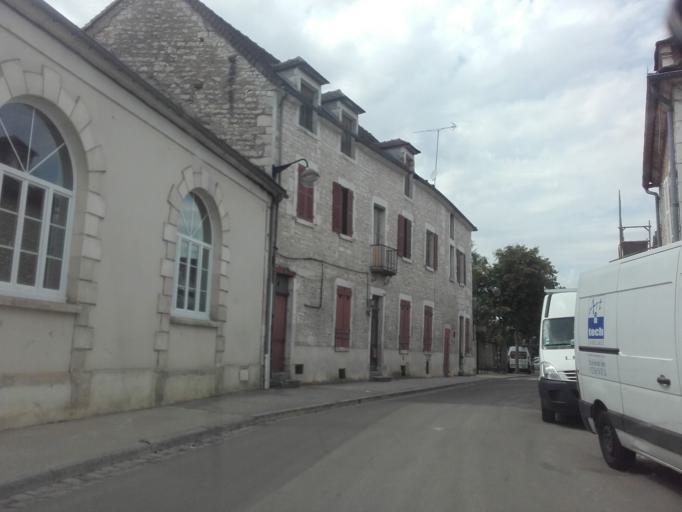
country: FR
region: Bourgogne
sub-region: Departement de l'Yonne
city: Chablis
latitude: 47.8139
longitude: 3.8002
